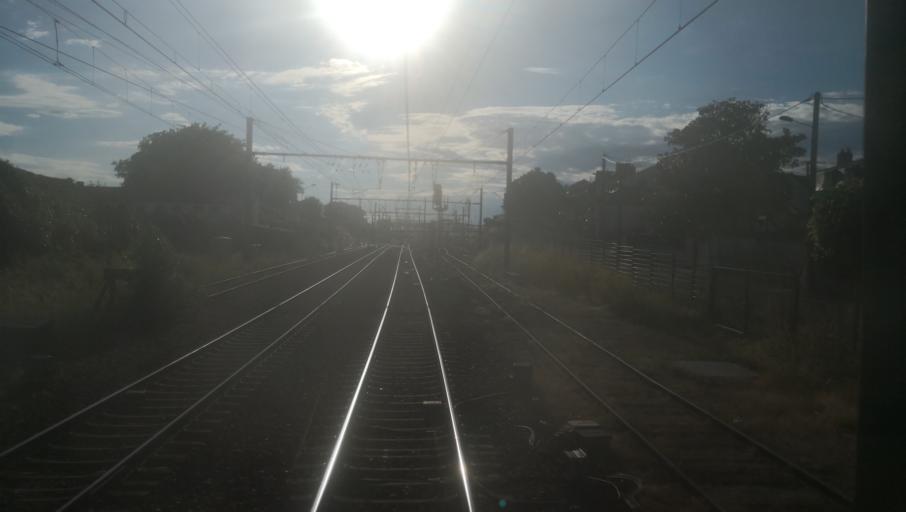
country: FR
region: Centre
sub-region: Departement du Cher
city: Vierzon
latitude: 47.2249
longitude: 2.0679
